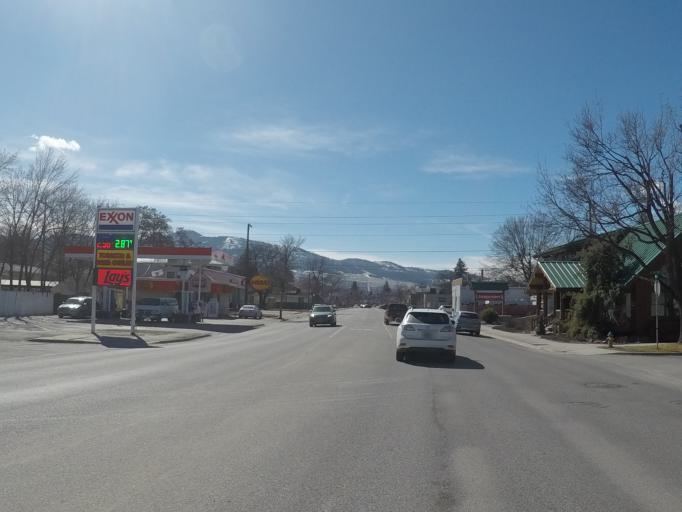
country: US
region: Montana
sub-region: Missoula County
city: Missoula
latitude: 46.8691
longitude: -114.0035
